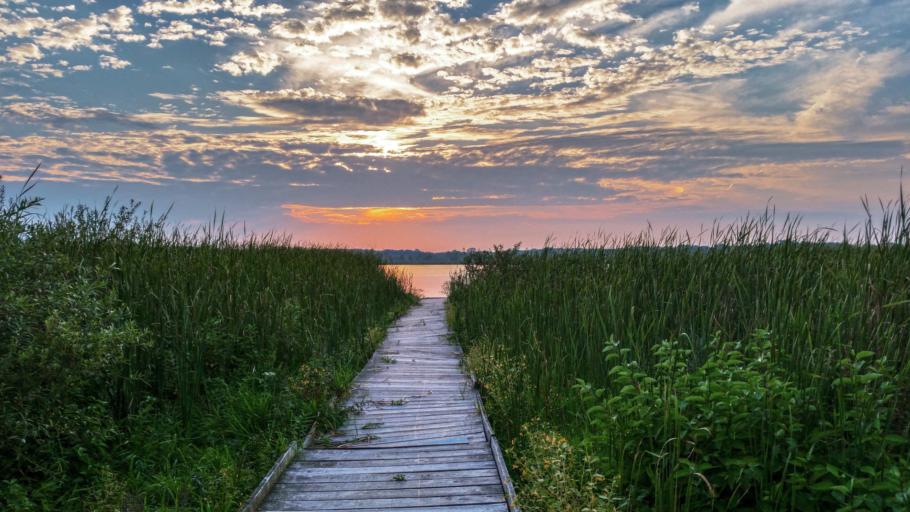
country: US
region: Wisconsin
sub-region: Jefferson County
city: Lake Mills
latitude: 43.0460
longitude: -88.9172
